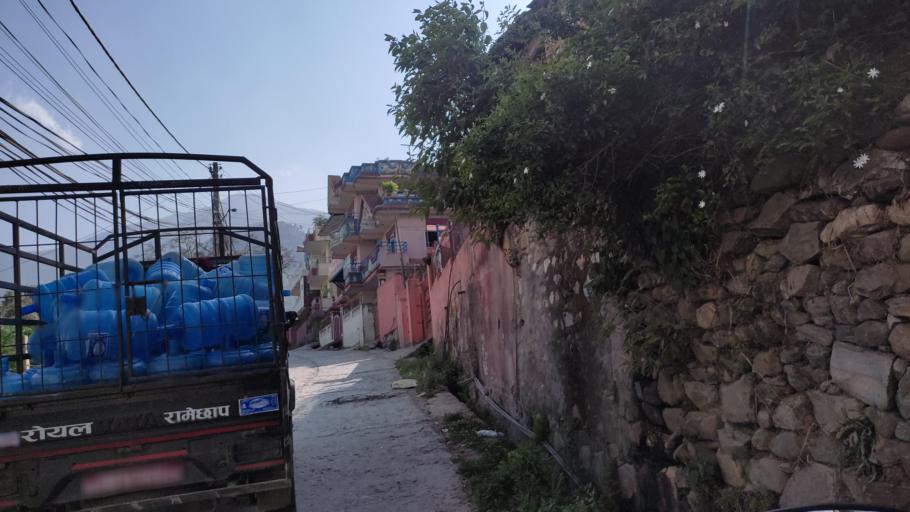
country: NP
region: Central Region
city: Kirtipur
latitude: 27.6728
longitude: 85.2515
